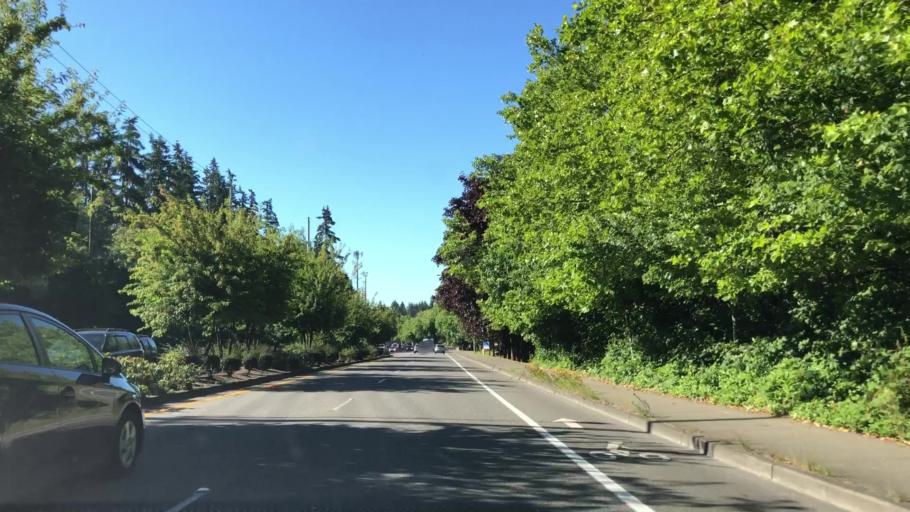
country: US
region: Washington
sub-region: Snohomish County
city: Mill Creek
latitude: 47.8539
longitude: -122.2183
